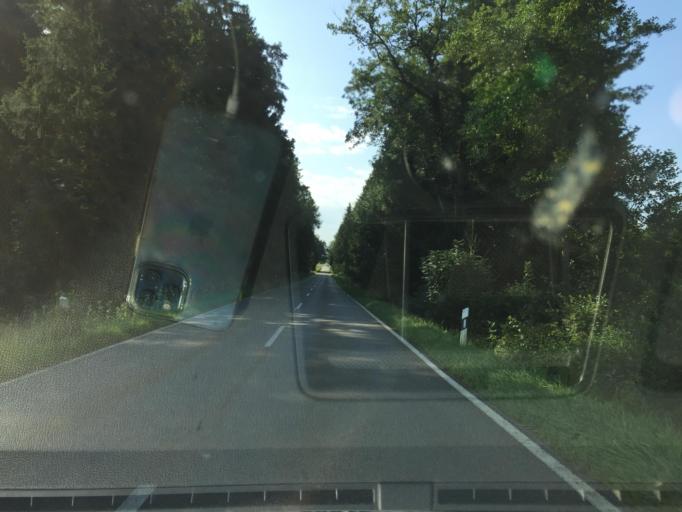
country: DE
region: Bavaria
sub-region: Upper Bavaria
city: Assling
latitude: 47.9689
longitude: 12.0093
